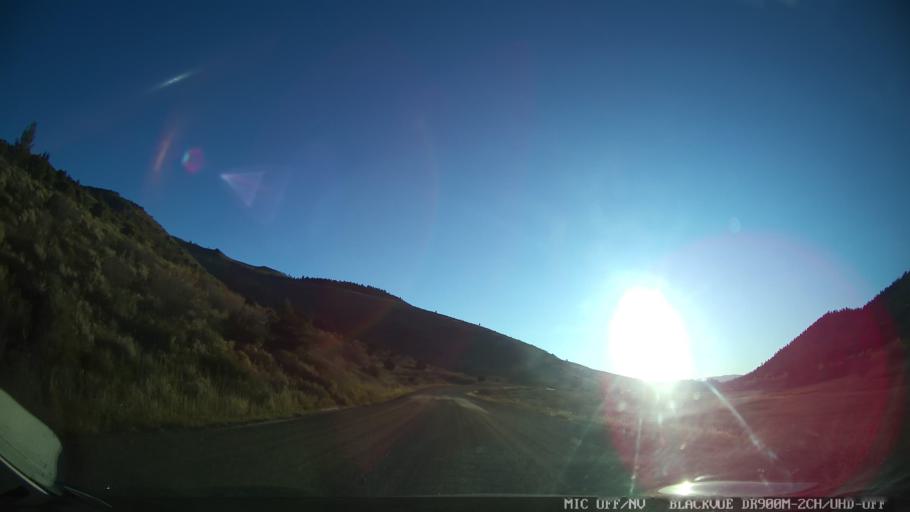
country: US
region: Colorado
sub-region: Grand County
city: Kremmling
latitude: 39.9935
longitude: -106.4617
